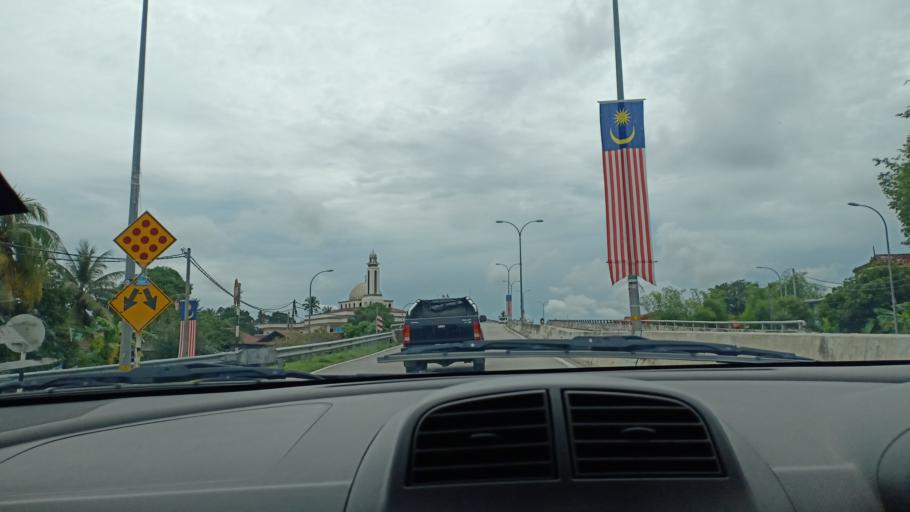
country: MY
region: Penang
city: Bukit Mertajam
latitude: 5.4072
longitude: 100.4751
